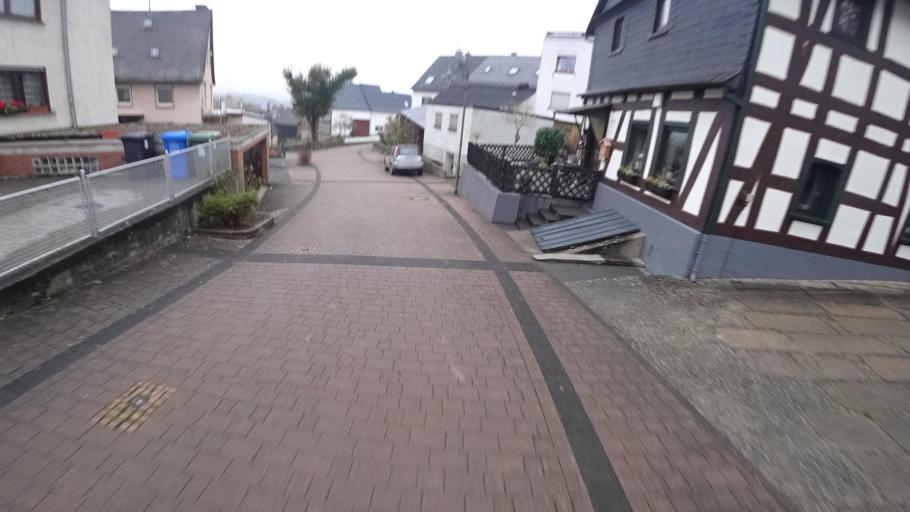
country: DE
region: Rheinland-Pfalz
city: Sankt Goar
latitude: 50.1457
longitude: 7.7085
